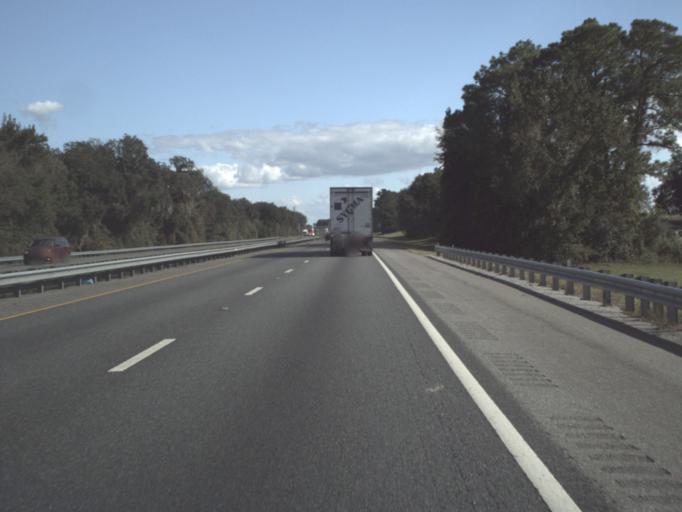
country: US
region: Florida
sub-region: Sumter County
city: Wildwood
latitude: 28.8081
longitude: -82.0082
